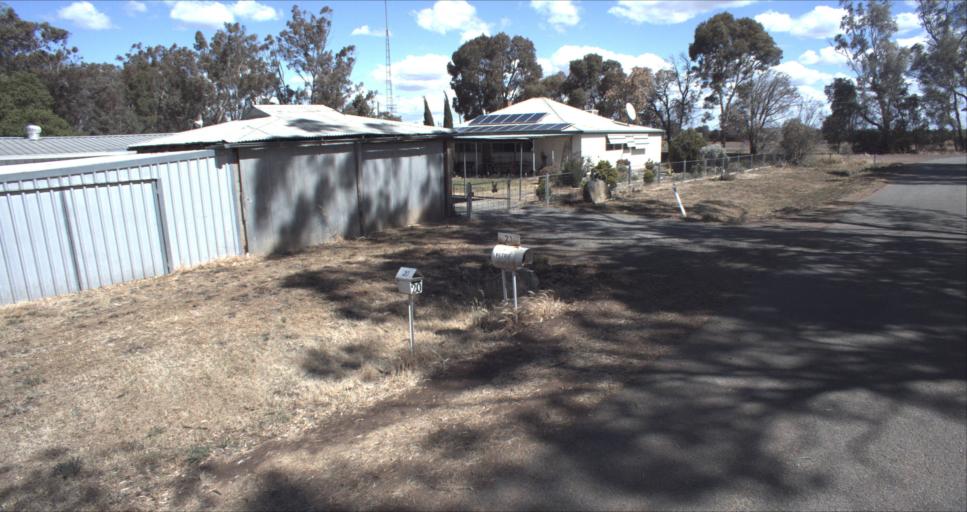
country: AU
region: New South Wales
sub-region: Leeton
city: Leeton
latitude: -34.5166
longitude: 146.2331
